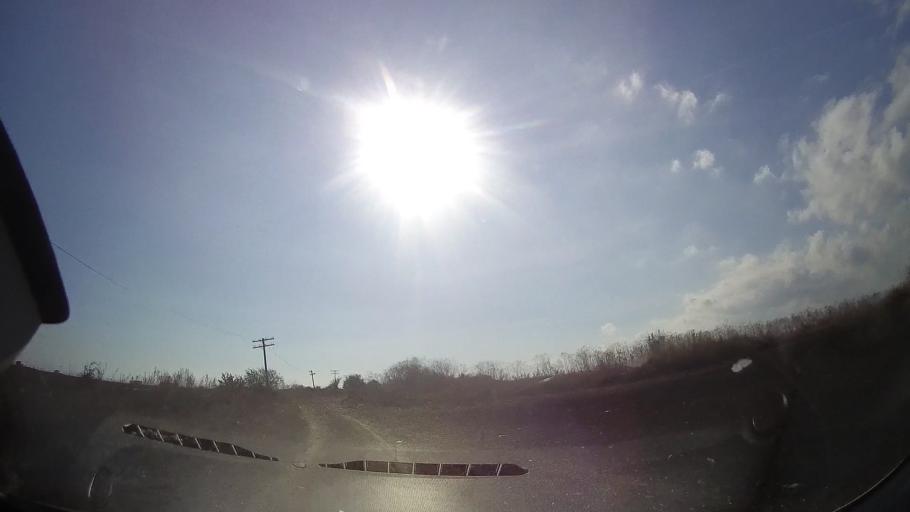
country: RO
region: Constanta
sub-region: Comuna Tuzla
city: Tuzla
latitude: 43.9756
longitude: 28.6440
